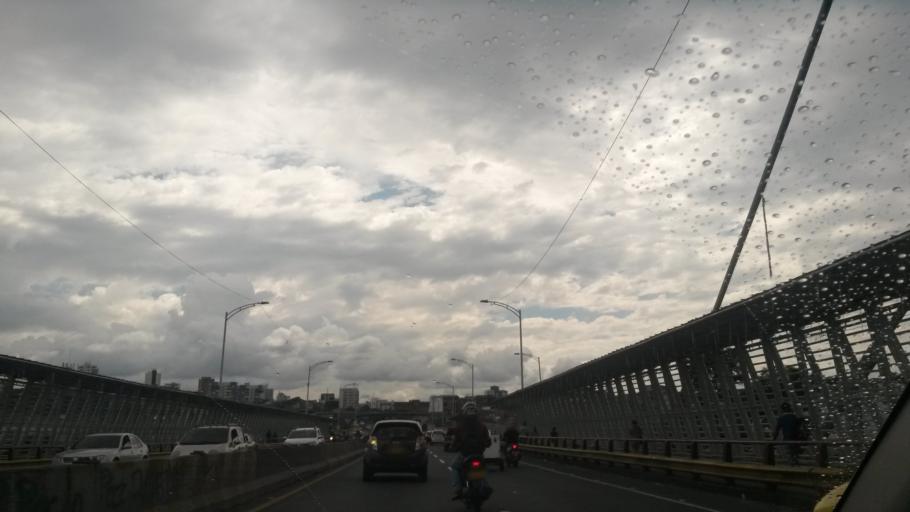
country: CO
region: Risaralda
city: Pereira
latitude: 4.8161
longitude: -75.6867
